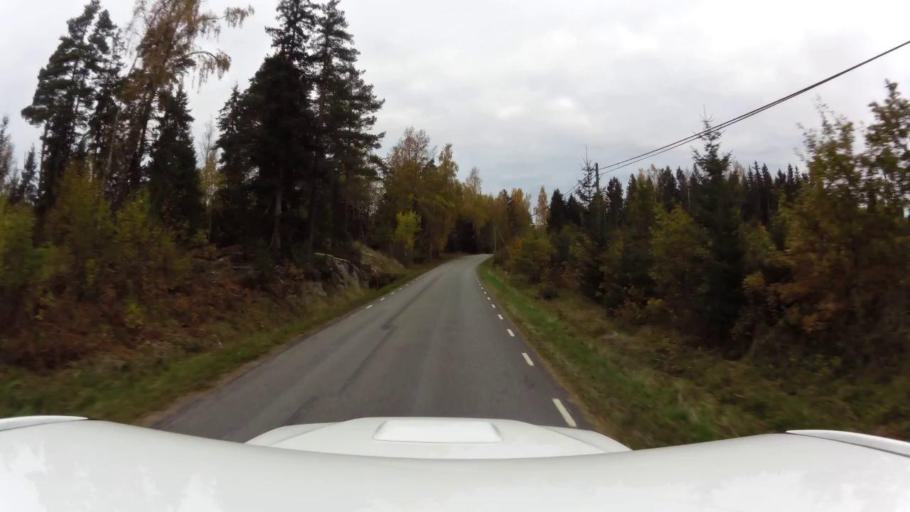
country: SE
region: OEstergoetland
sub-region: Linkopings Kommun
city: Ljungsbro
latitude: 58.5462
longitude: 15.4144
